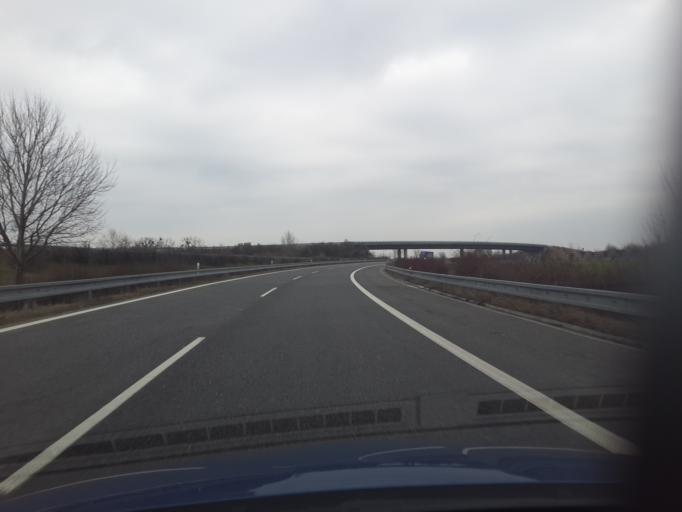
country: AT
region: Burgenland
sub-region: Politischer Bezirk Neusiedl am See
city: Kittsee
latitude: 48.0738
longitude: 17.1004
